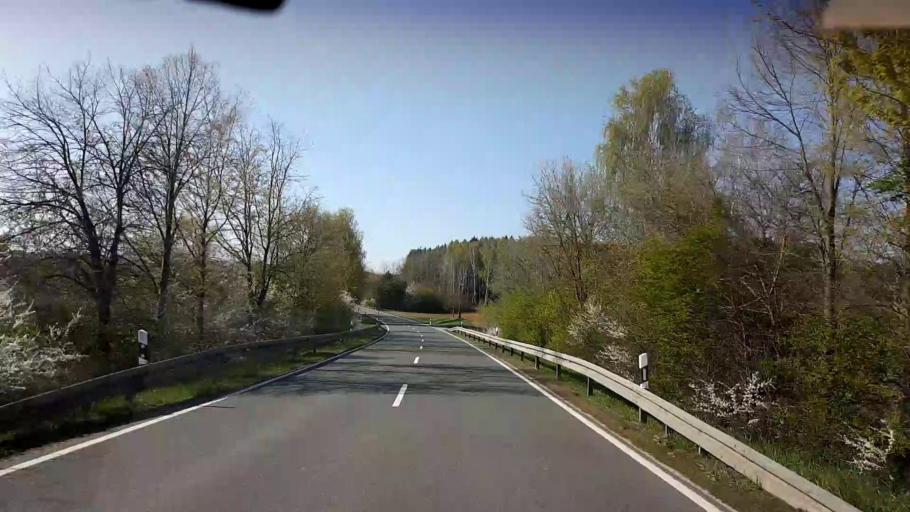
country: DE
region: Bavaria
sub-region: Upper Franconia
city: Stadelhofen
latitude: 49.9896
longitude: 11.2265
